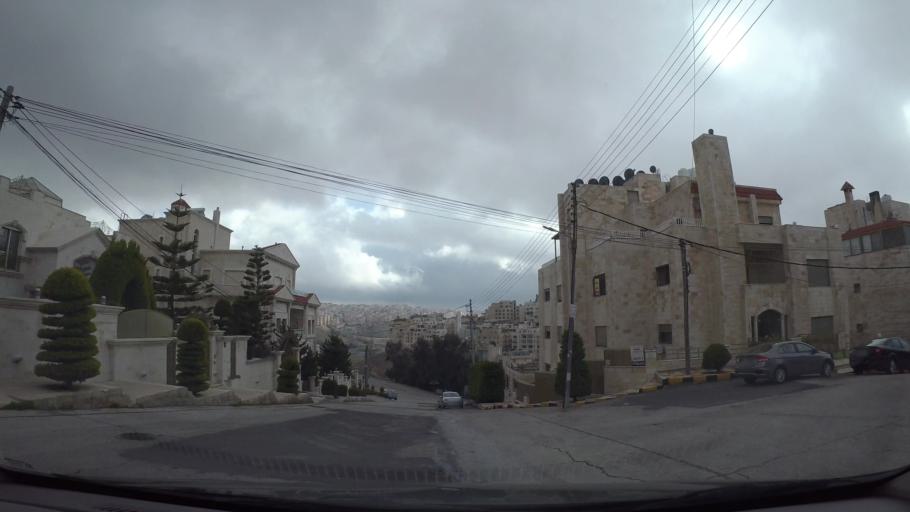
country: JO
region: Amman
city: Amman
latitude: 31.9429
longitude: 35.8996
